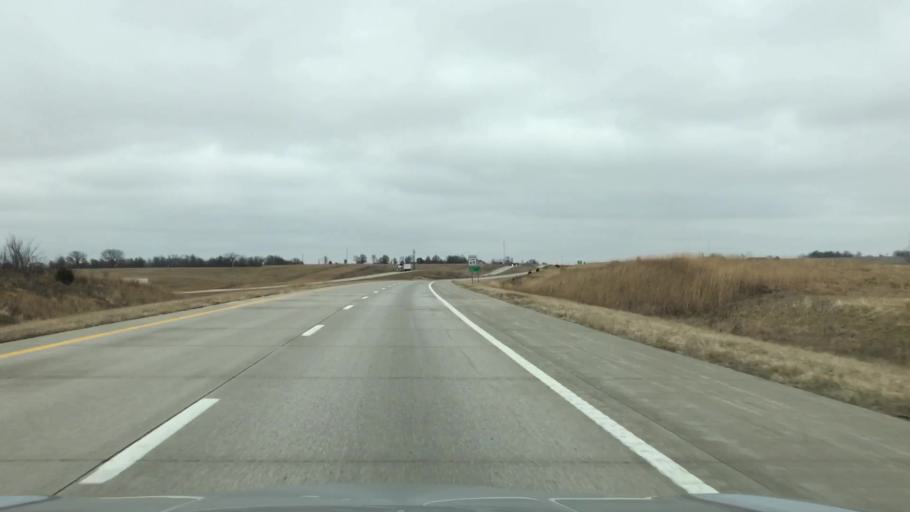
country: US
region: Missouri
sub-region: Linn County
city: Marceline
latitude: 39.7643
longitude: -92.7890
